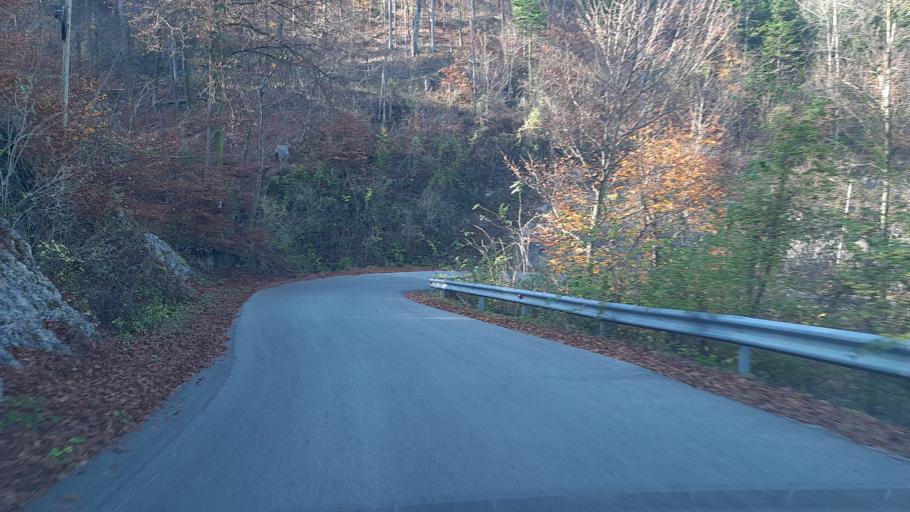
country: SI
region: Borovnica
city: Borovnica
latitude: 45.9047
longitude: 14.3633
